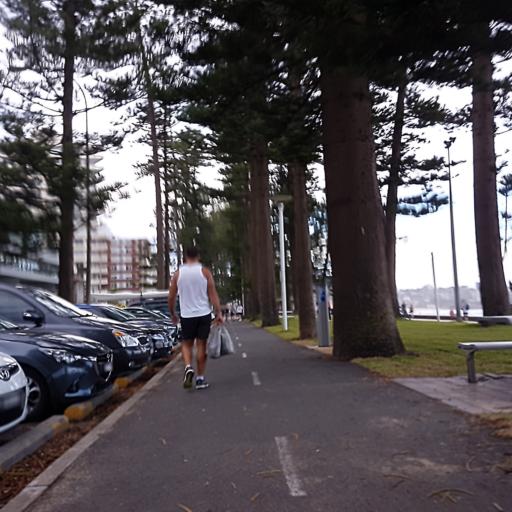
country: AU
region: New South Wales
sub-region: Manly Vale
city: Manly
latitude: -33.7955
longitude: 151.2875
